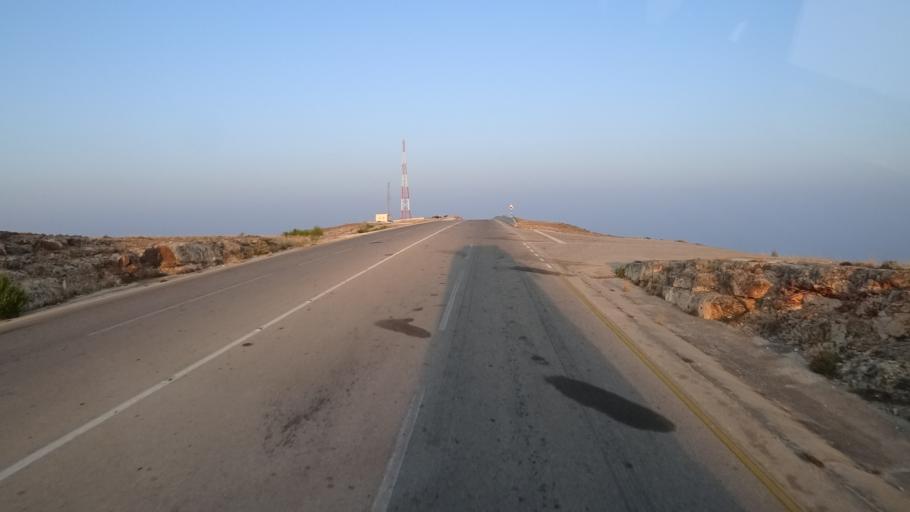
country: OM
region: Zufar
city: Salalah
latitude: 16.8250
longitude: 53.6484
